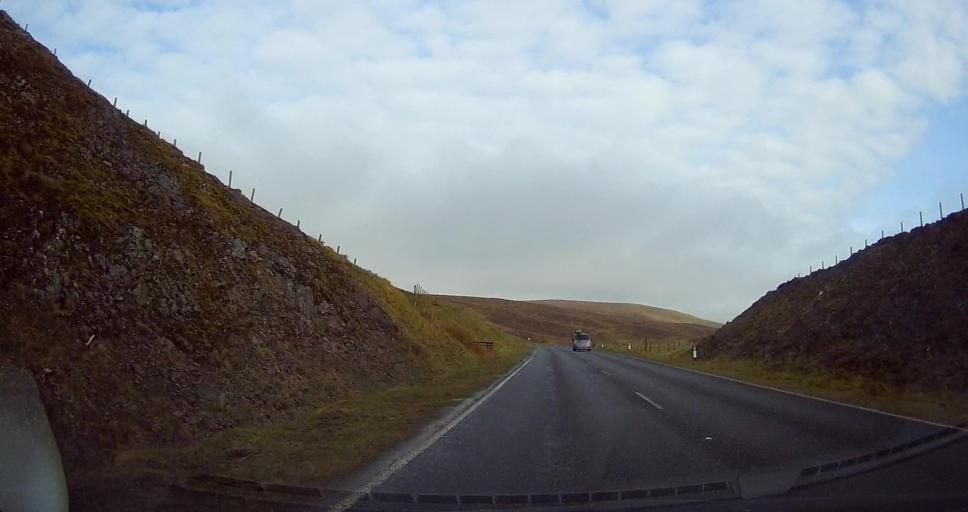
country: GB
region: Scotland
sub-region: Shetland Islands
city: Sandwick
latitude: 60.0682
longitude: -1.2263
